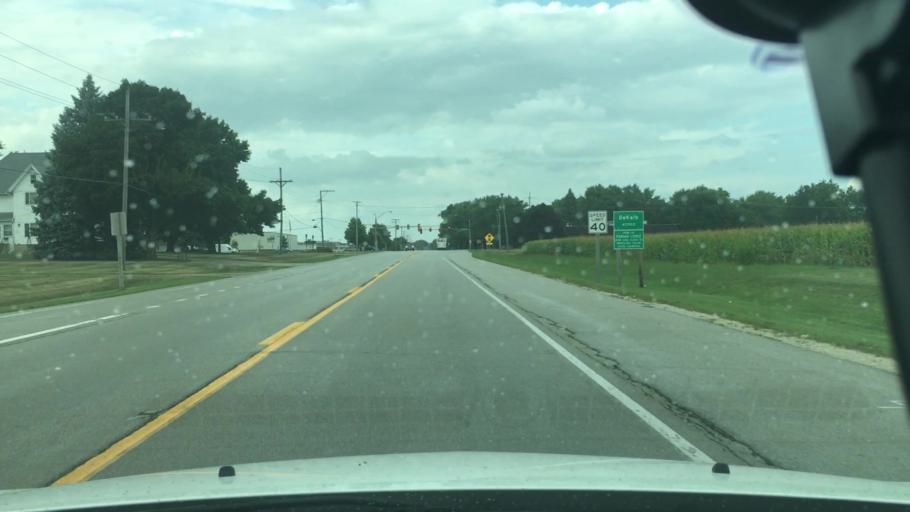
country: US
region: Illinois
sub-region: DeKalb County
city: DeKalb
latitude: 41.9050
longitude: -88.7535
